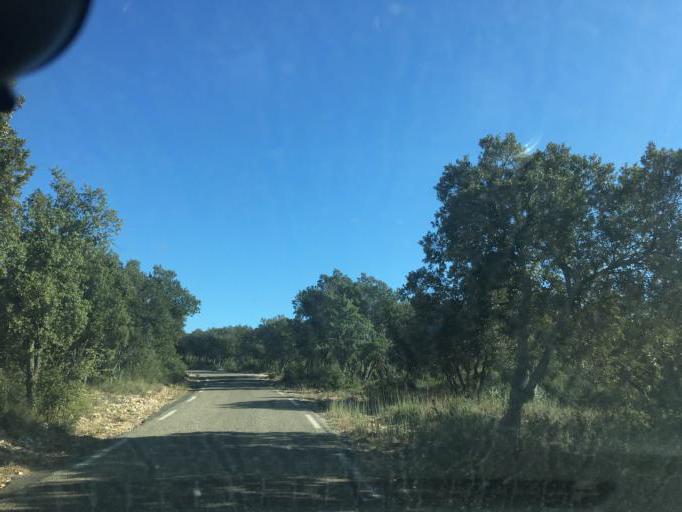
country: FR
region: Provence-Alpes-Cote d'Azur
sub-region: Departement du Var
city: Regusse
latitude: 43.7338
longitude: 6.1041
